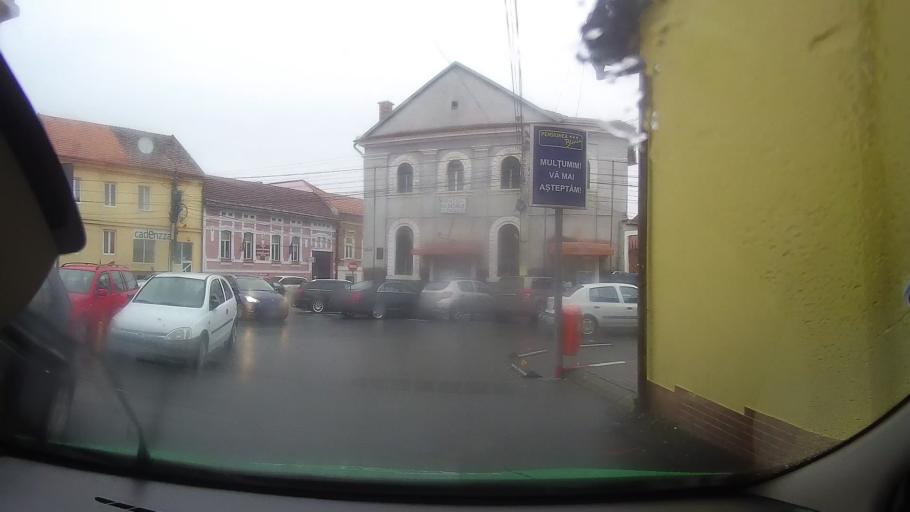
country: RO
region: Mures
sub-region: Municipiul Reghin
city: Reghin
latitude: 46.7802
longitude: 24.7024
